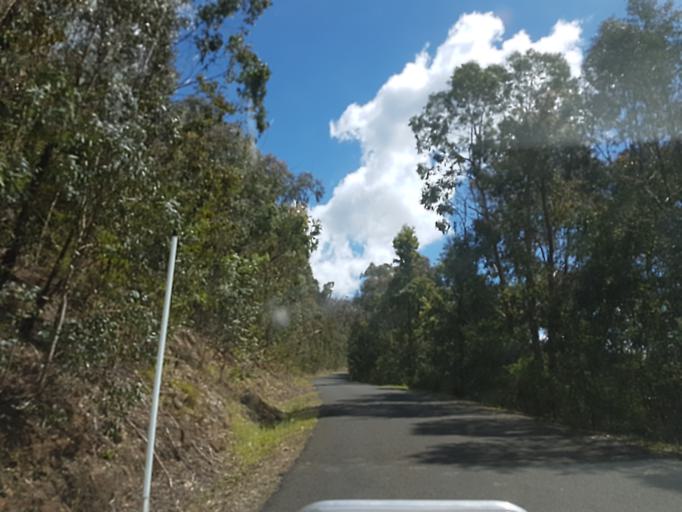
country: AU
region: Victoria
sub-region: East Gippsland
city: Bairnsdale
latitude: -37.4008
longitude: 147.2458
